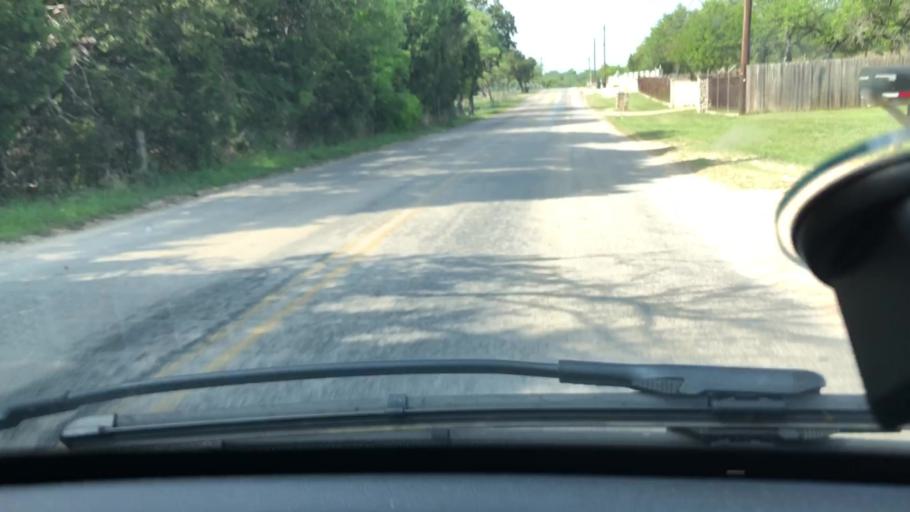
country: US
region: Texas
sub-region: Comal County
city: Bulverde
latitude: 29.7699
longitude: -98.4588
